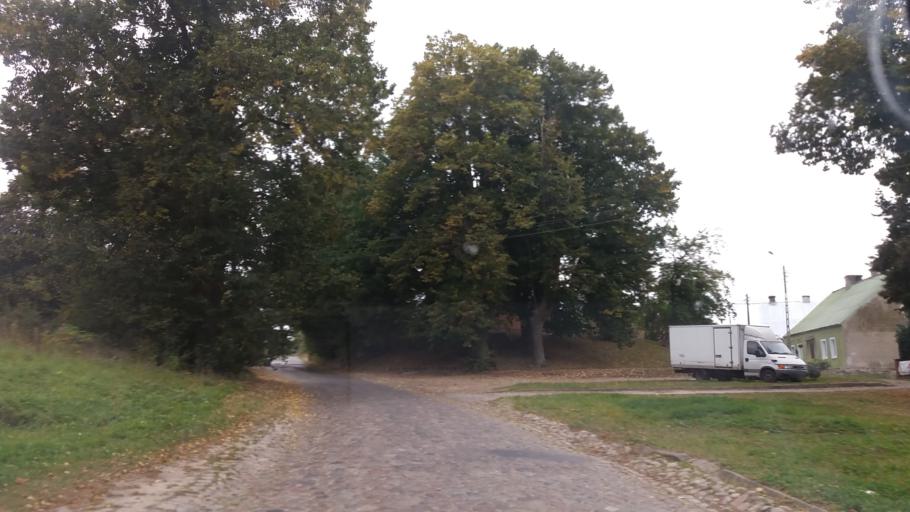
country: PL
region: West Pomeranian Voivodeship
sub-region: Powiat choszczenski
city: Bierzwnik
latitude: 52.9994
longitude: 15.5938
